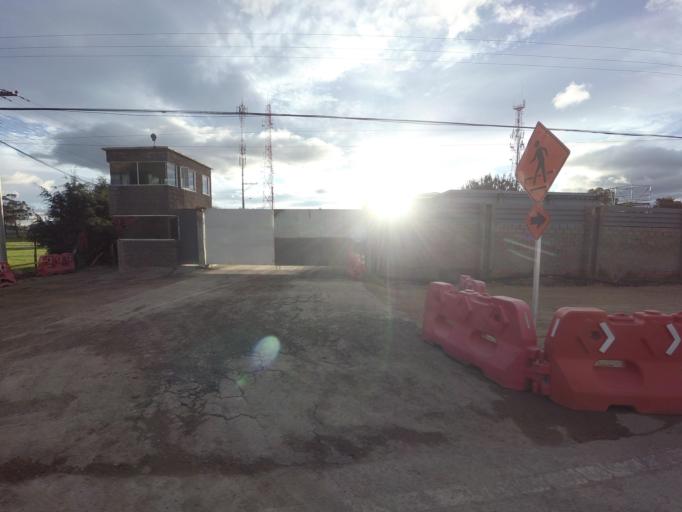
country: CO
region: Cundinamarca
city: Chia
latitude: 4.8378
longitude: -74.0288
